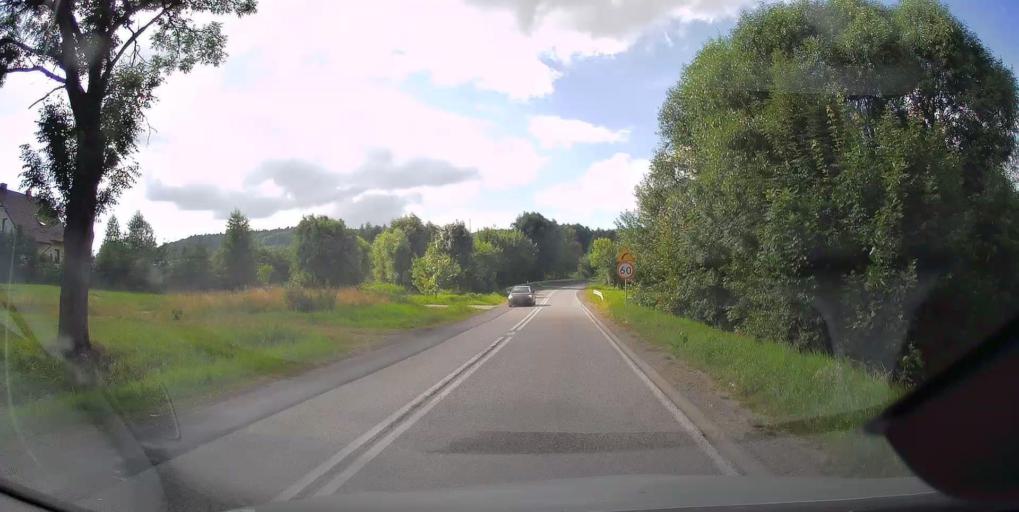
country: PL
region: Swietokrzyskie
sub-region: Powiat kielecki
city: Nowa Slupia
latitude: 50.8482
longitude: 21.0862
